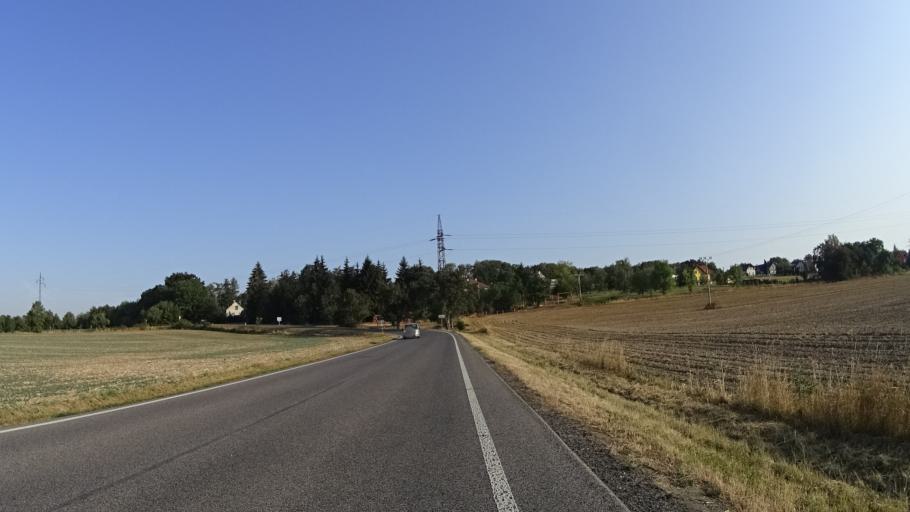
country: CZ
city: Ohrazenice
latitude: 50.5908
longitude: 15.1129
